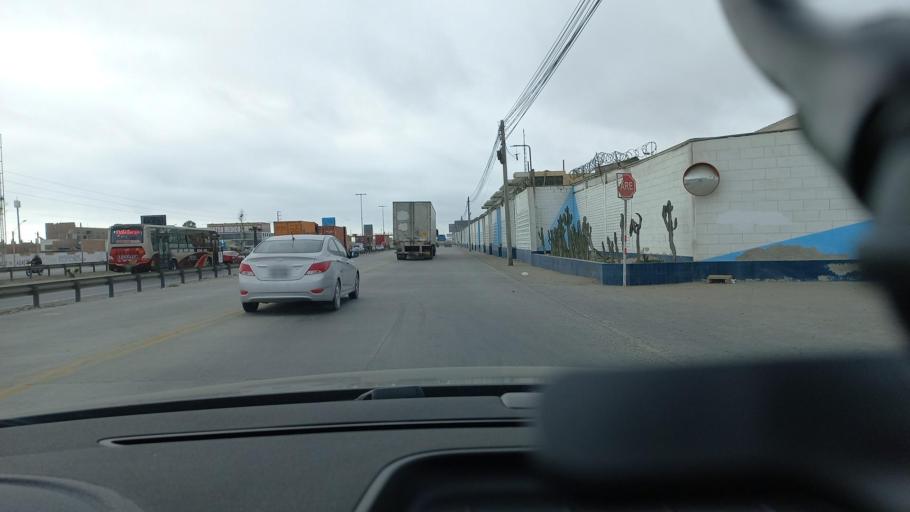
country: PE
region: Lima
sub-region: Lima
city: Surco
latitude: -12.2380
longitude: -76.9517
